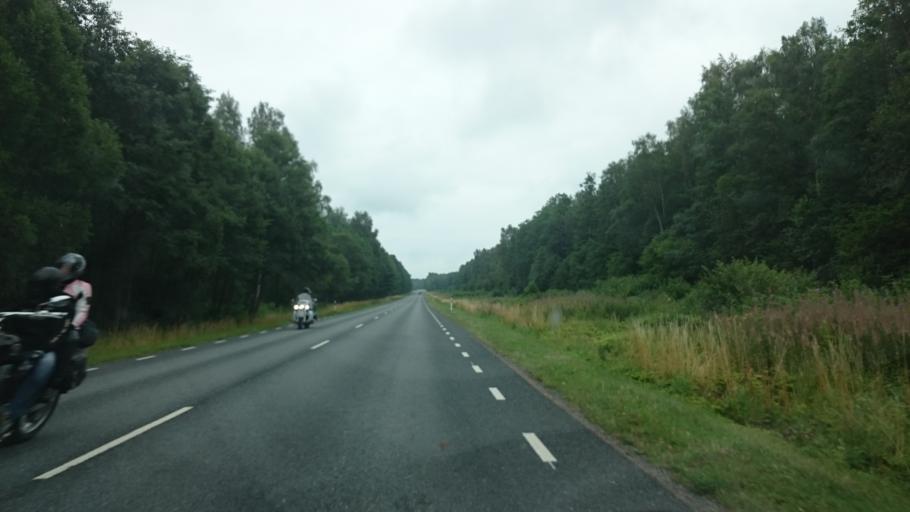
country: EE
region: Saare
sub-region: Orissaare vald
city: Orissaare
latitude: 58.6058
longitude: 23.2964
